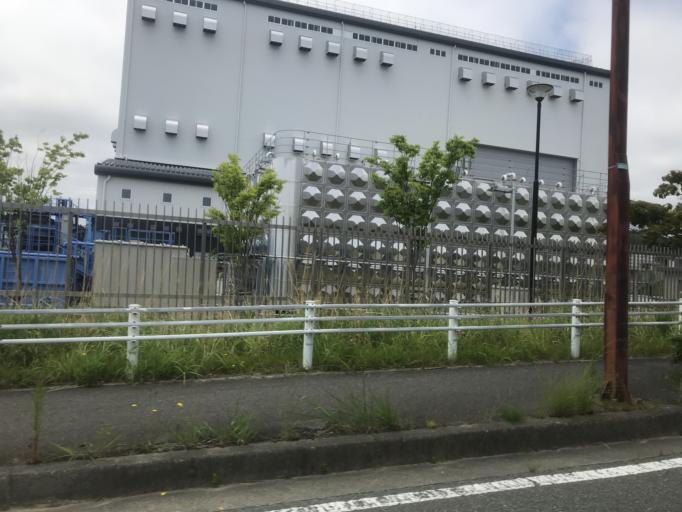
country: JP
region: Fukushima
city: Iwaki
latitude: 37.2449
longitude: 140.9906
